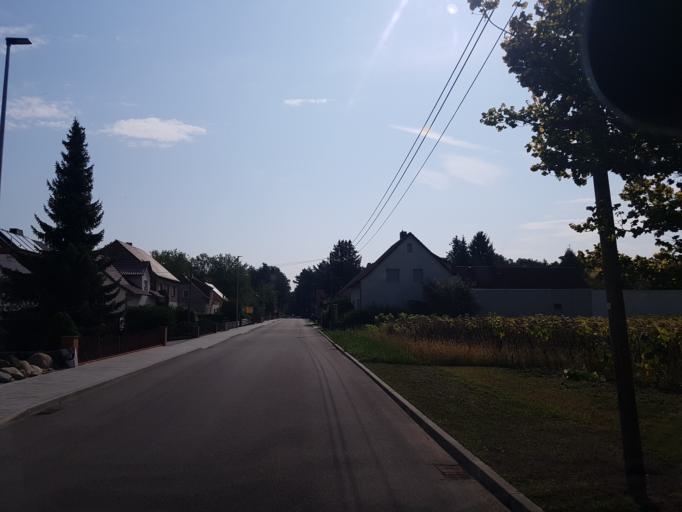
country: DE
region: Brandenburg
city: Plessa
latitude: 51.5320
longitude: 13.6791
